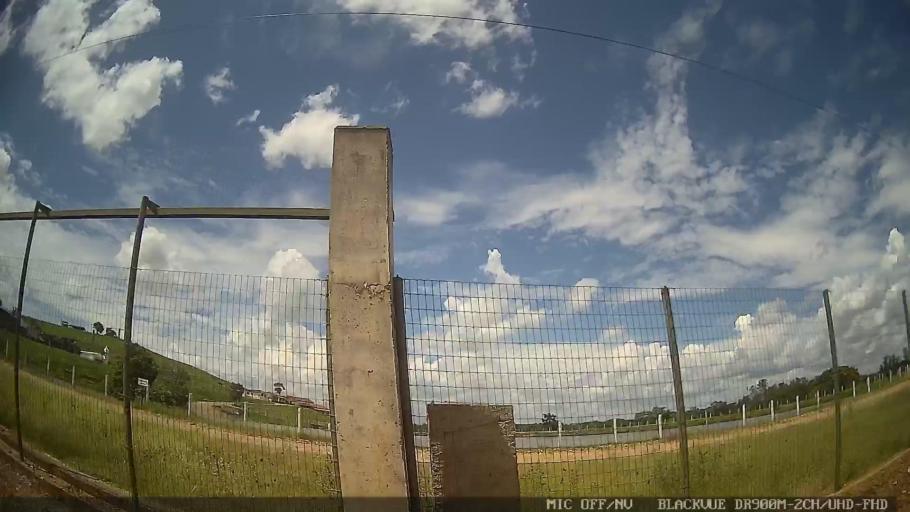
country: BR
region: Sao Paulo
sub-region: Conchas
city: Conchas
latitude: -23.0534
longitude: -47.9850
